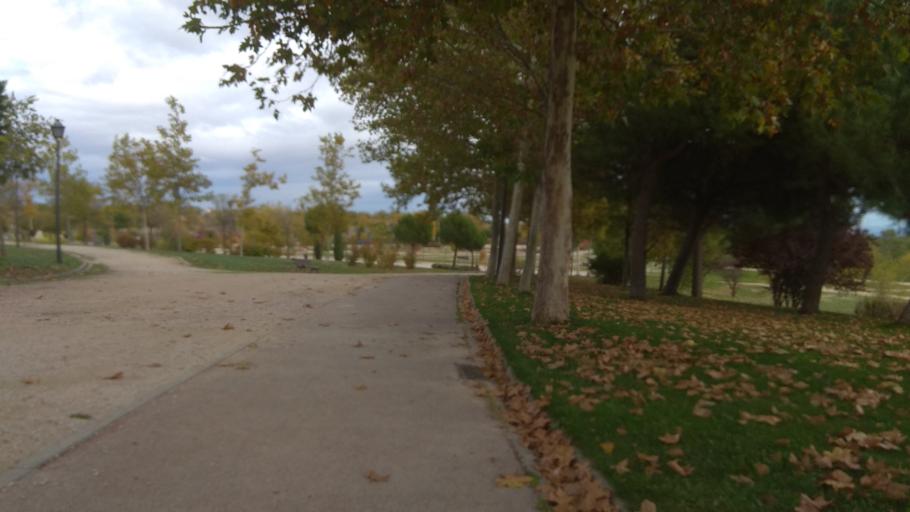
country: ES
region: Madrid
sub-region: Provincia de Madrid
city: Vicalvaro
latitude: 40.4114
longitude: -3.6153
